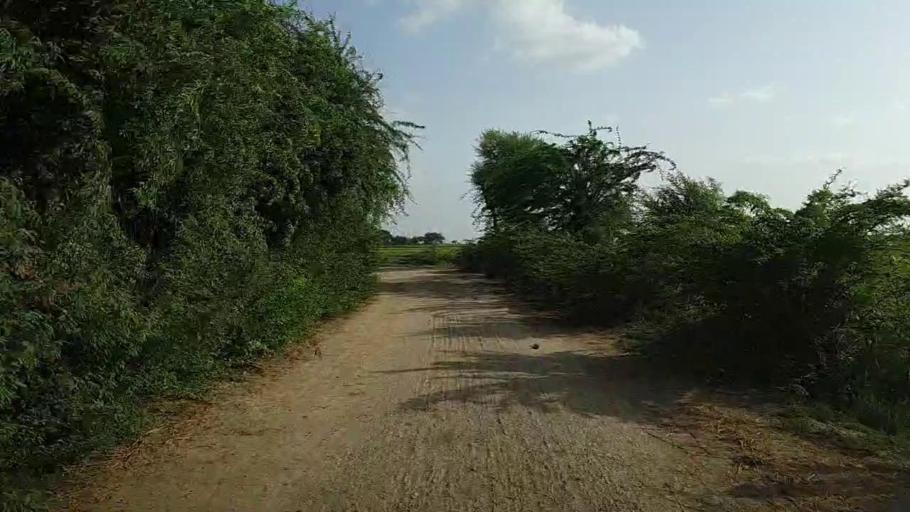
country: PK
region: Sindh
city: Kario
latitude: 24.6495
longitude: 68.4982
